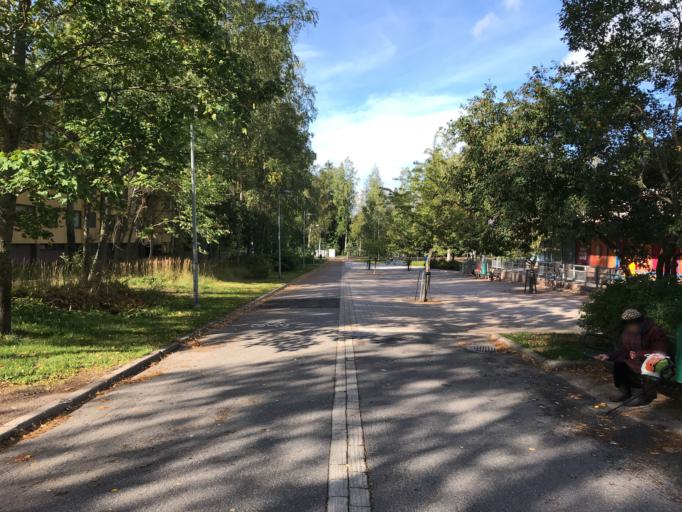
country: FI
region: Uusimaa
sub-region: Helsinki
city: Vantaa
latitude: 60.2235
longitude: 25.0602
